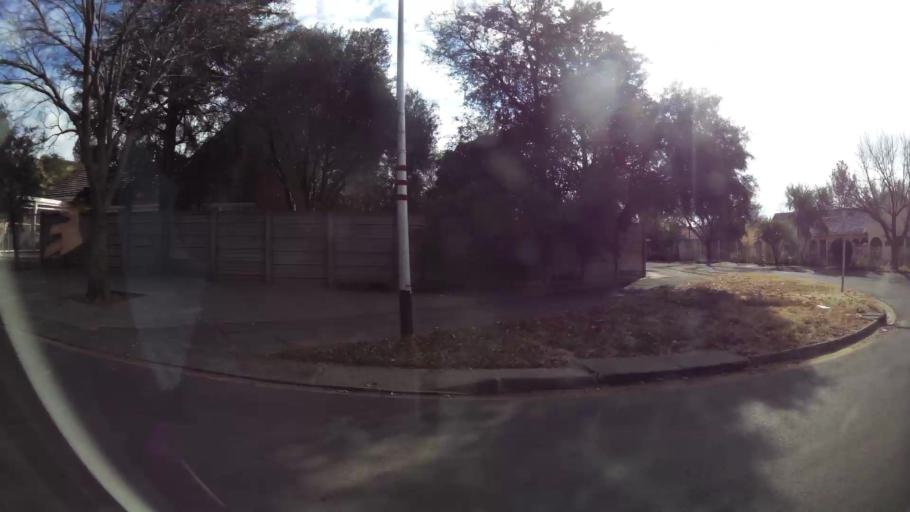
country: ZA
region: Orange Free State
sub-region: Mangaung Metropolitan Municipality
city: Bloemfontein
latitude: -29.0775
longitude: 26.2401
